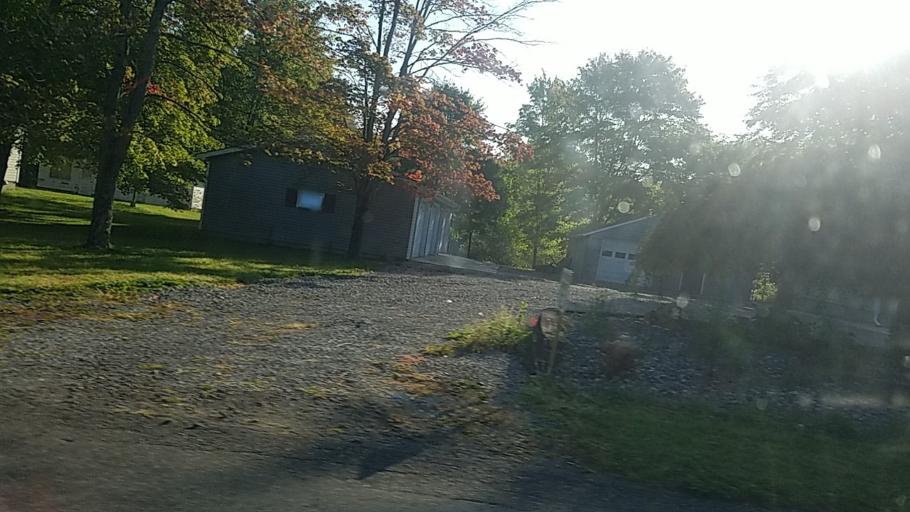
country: US
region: Ohio
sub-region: Trumbull County
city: Niles
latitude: 41.1640
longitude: -80.7535
